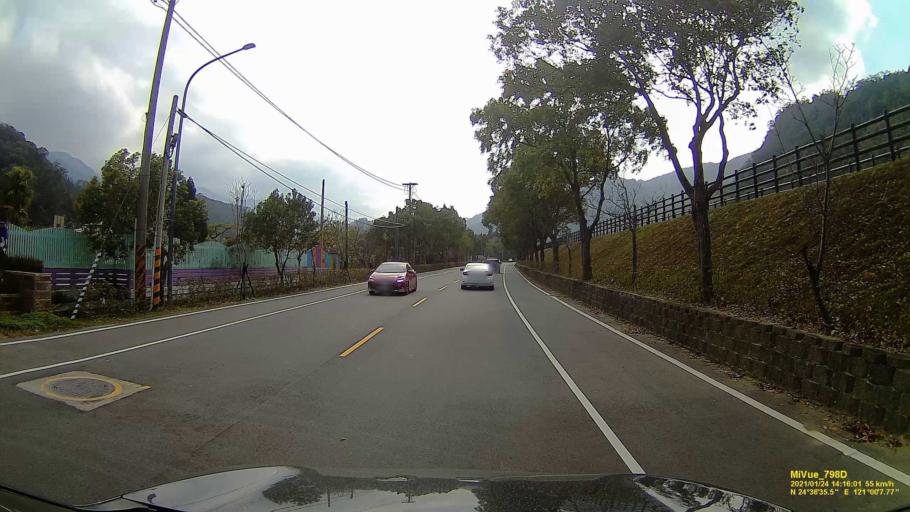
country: TW
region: Taiwan
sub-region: Miaoli
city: Miaoli
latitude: 24.6095
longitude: 121.0020
